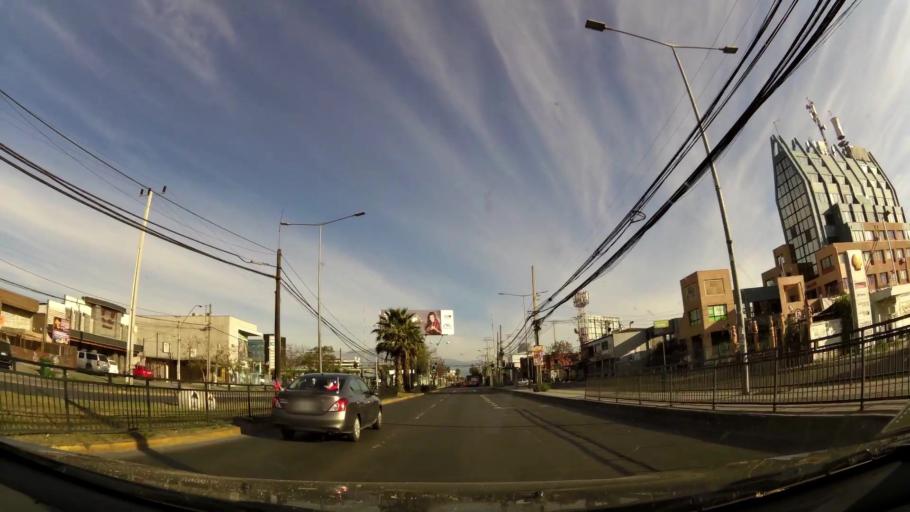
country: CL
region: Santiago Metropolitan
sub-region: Provincia de Cordillera
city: Puente Alto
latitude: -33.6051
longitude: -70.5767
